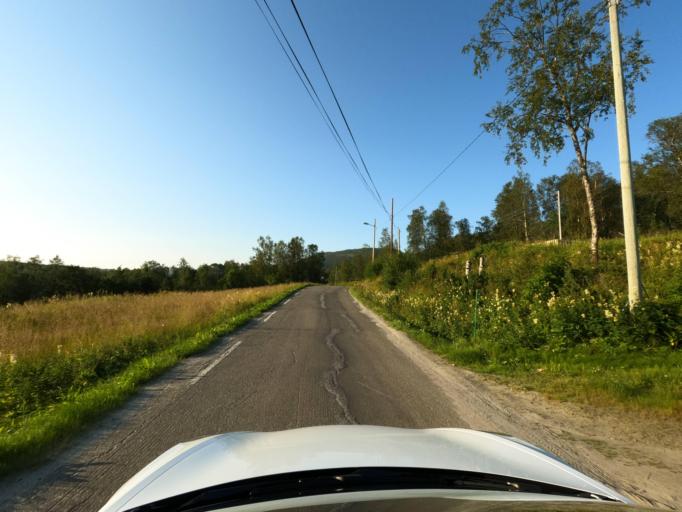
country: NO
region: Nordland
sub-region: Ballangen
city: Ballangen
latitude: 68.5250
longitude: 16.7659
